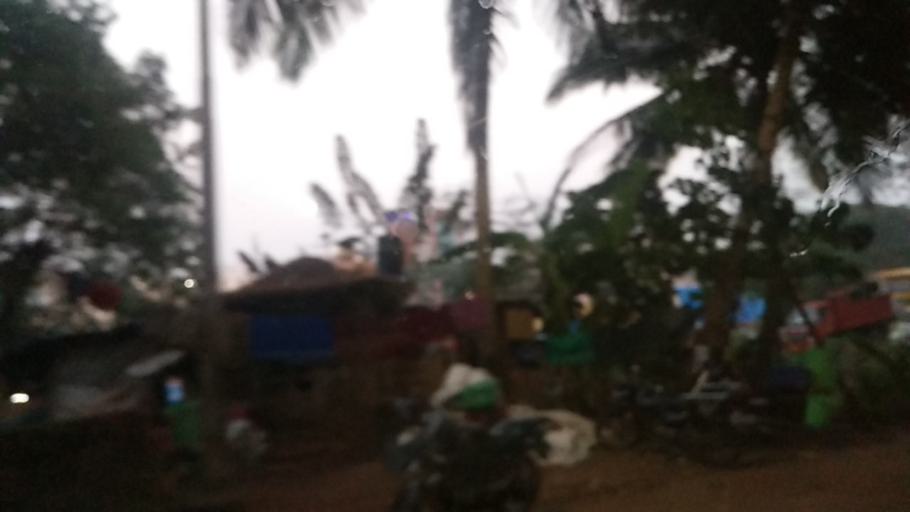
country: IN
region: Goa
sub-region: South Goa
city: Madgaon
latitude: 15.2843
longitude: 73.9555
